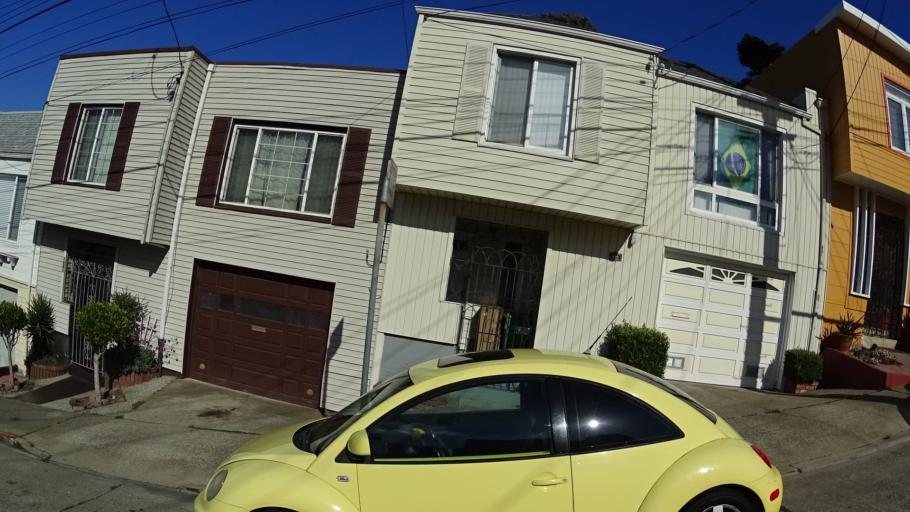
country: US
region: California
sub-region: San Mateo County
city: Brisbane
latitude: 37.7204
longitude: -122.4093
